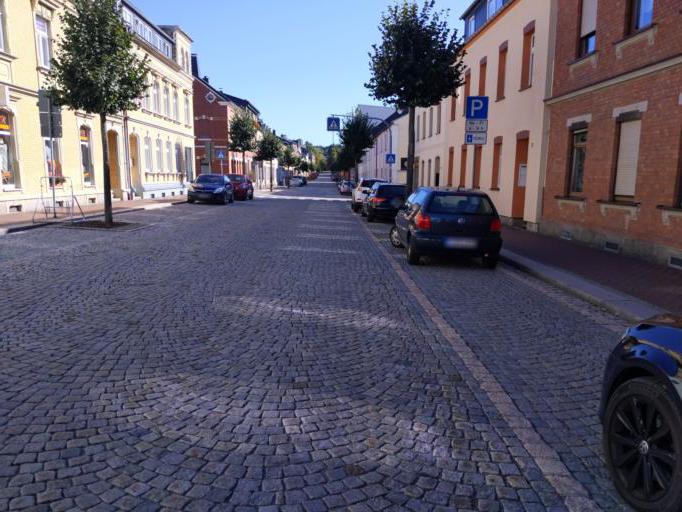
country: DE
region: Saxony
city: Pohl
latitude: 50.3943
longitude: 12.3326
